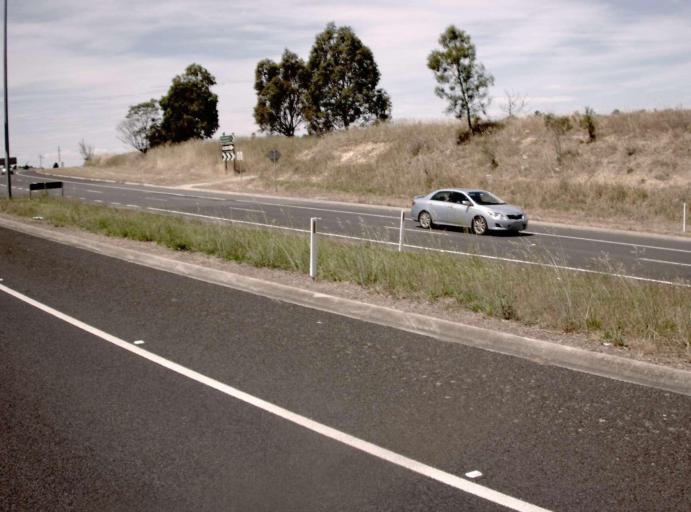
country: AU
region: Victoria
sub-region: Wellington
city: Heyfield
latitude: -38.1384
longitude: 146.7941
